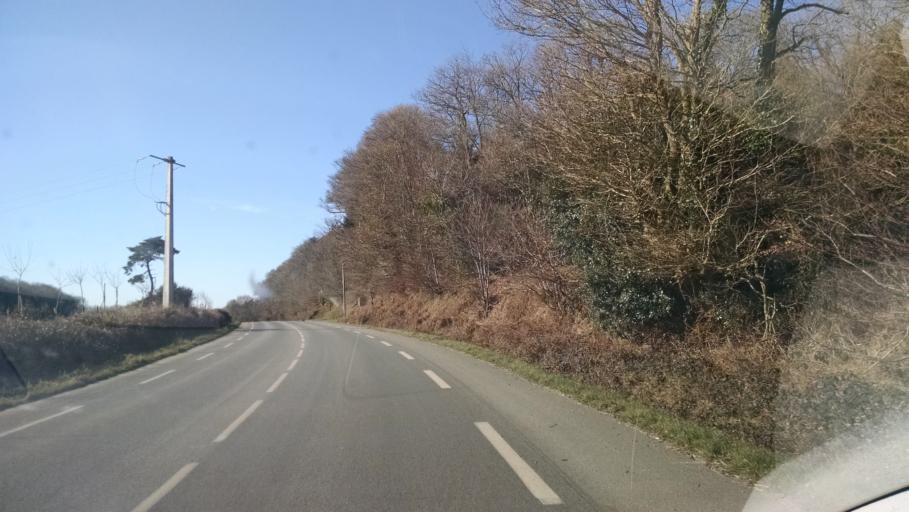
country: FR
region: Brittany
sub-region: Departement du Morbihan
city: Gestel
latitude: 47.8052
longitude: -3.4729
